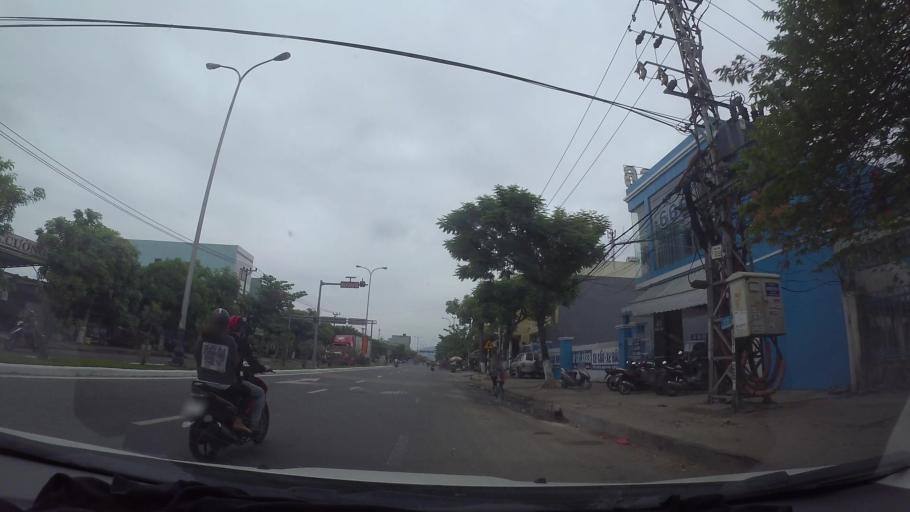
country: VN
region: Da Nang
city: Lien Chieu
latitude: 16.0847
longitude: 108.1451
